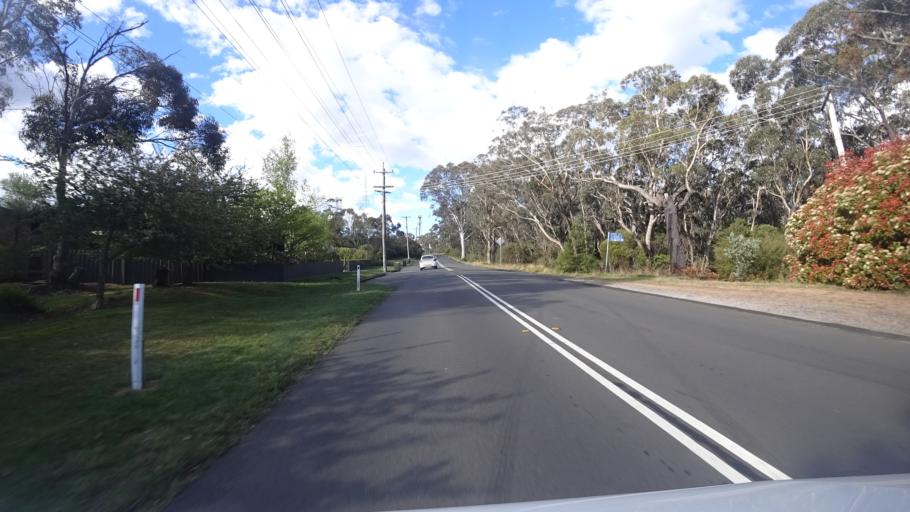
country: AU
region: New South Wales
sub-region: Blue Mountains Municipality
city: Katoomba
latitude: -33.7119
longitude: 150.2988
